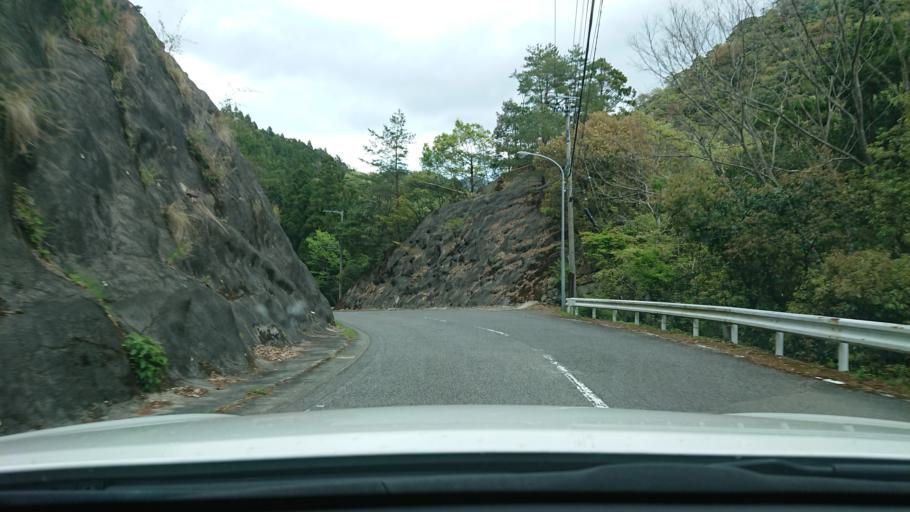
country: JP
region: Tokushima
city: Ishii
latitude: 33.9110
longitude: 134.4210
